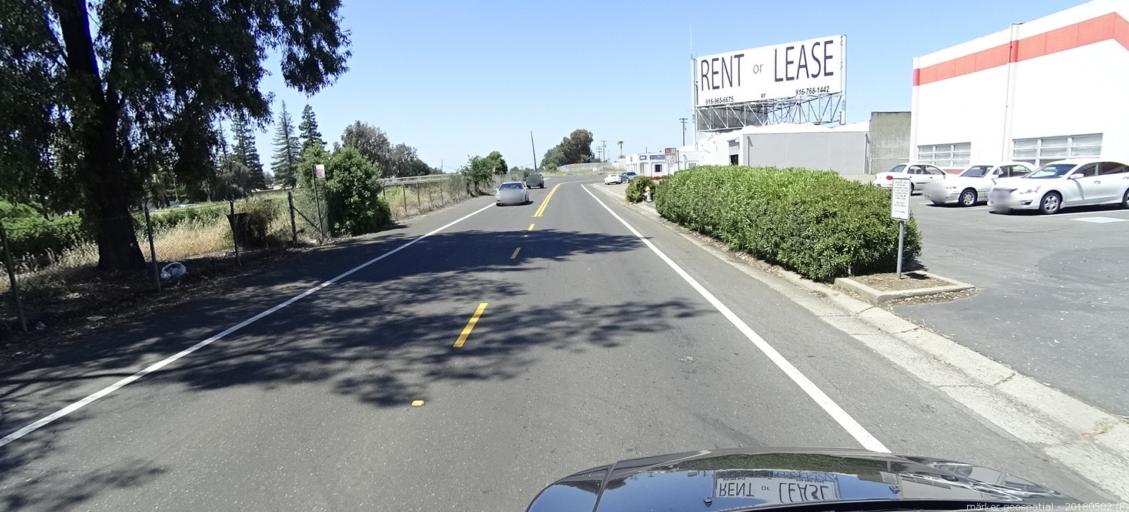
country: US
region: California
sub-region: Sacramento County
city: Sacramento
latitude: 38.6004
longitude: -121.4446
